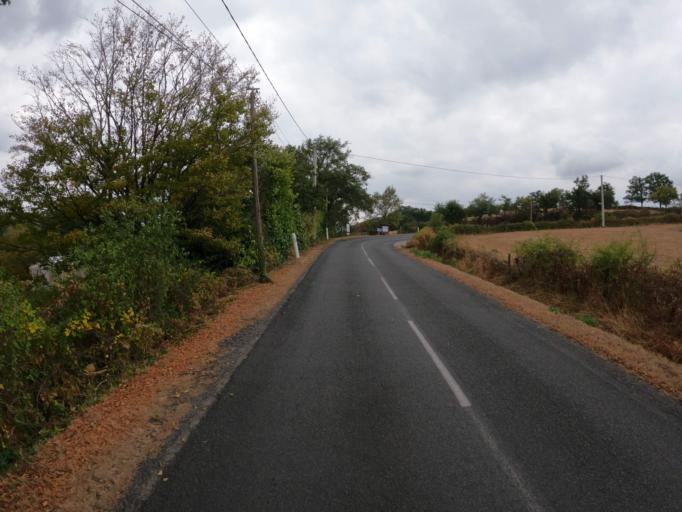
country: FR
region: Pays de la Loire
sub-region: Departement de Maine-et-Loire
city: Le Longeron
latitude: 47.0113
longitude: -1.0744
